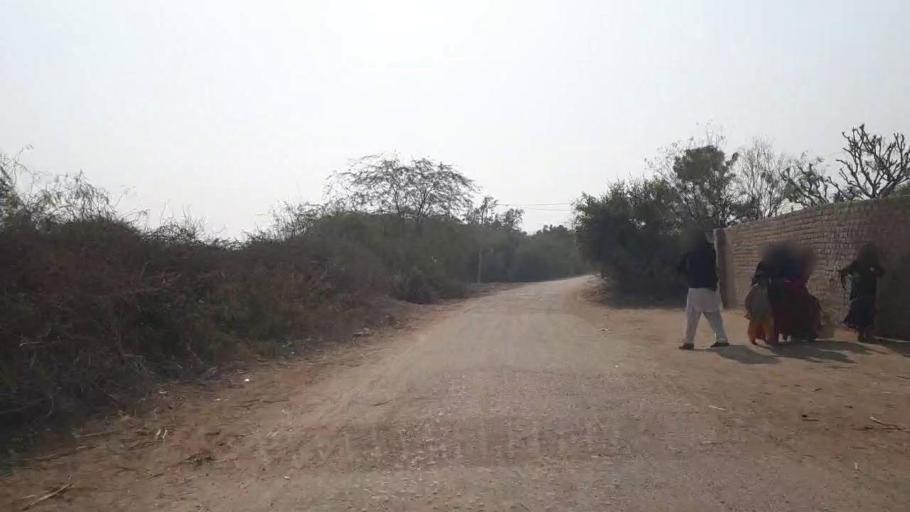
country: PK
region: Sindh
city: Hala
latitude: 25.8936
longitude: 68.4413
